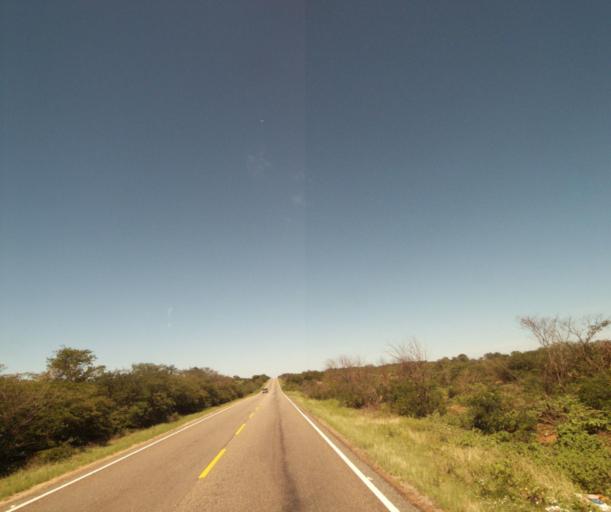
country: BR
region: Bahia
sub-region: Palmas De Monte Alto
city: Palmas de Monte Alto
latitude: -14.2530
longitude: -43.2056
